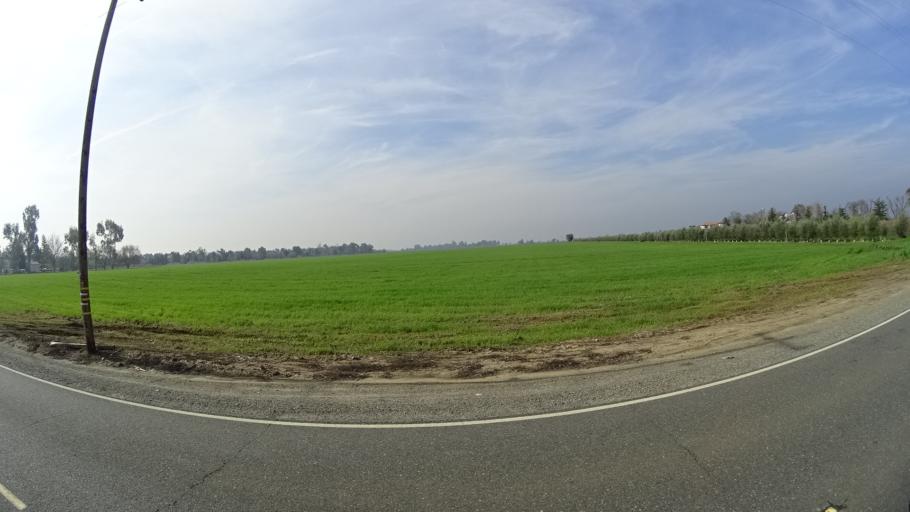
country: US
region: California
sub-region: Yolo County
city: Davis
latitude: 38.5782
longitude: -121.7486
